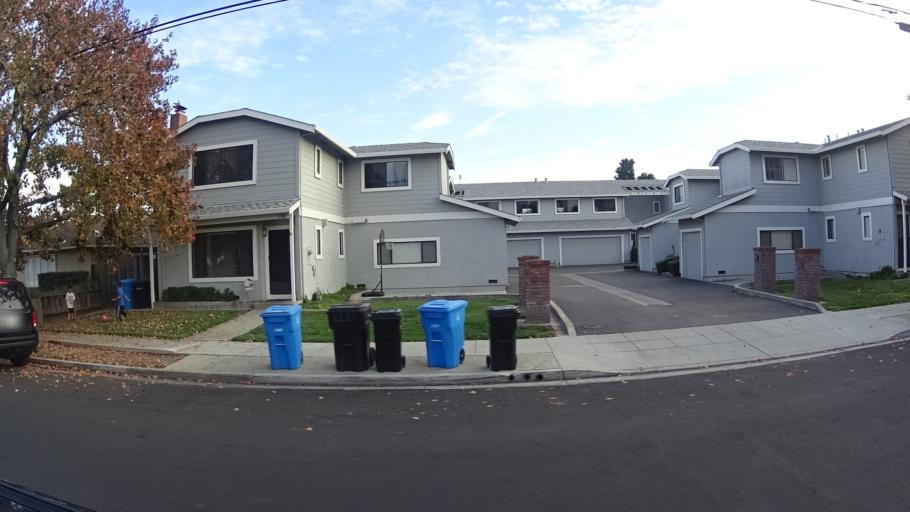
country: US
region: California
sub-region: Santa Clara County
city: Santa Clara
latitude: 37.3497
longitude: -121.9544
